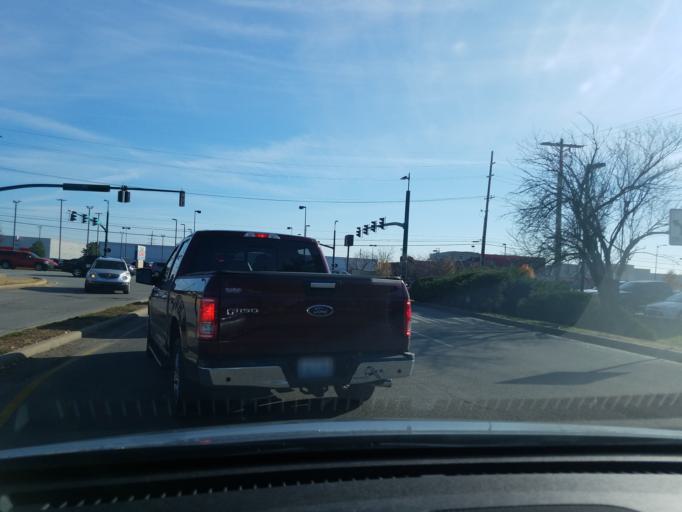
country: US
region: Indiana
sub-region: Clark County
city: Clarksville
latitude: 38.3172
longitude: -85.7574
